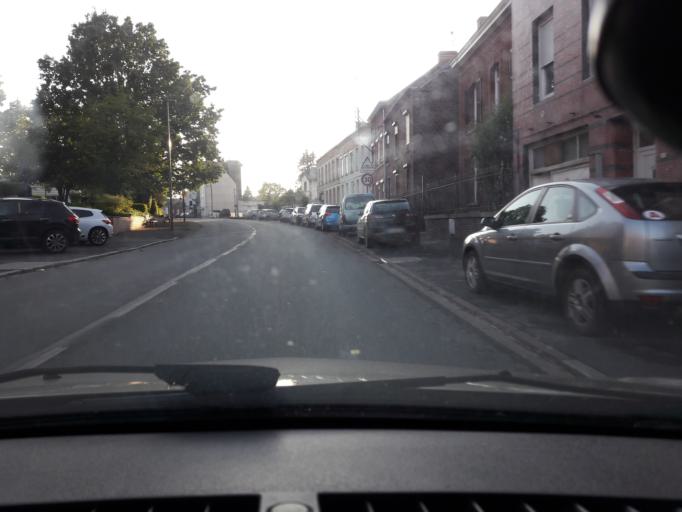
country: FR
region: Nord-Pas-de-Calais
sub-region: Departement du Nord
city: Jeumont
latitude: 50.2958
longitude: 4.0918
